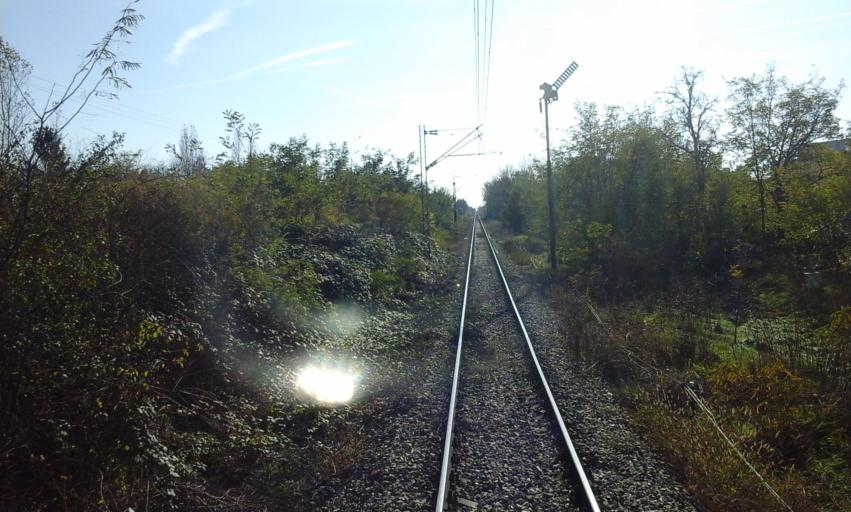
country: RS
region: Autonomna Pokrajina Vojvodina
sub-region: Severnobacki Okrug
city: Subotica
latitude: 46.0691
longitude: 19.6882
